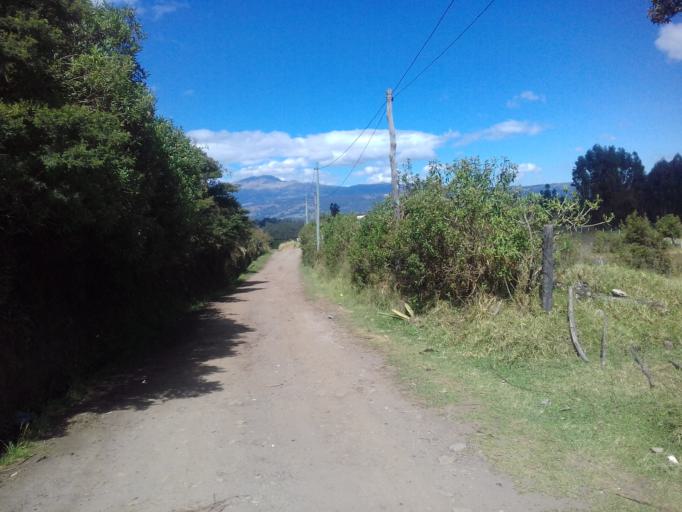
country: EC
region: Pichincha
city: Sangolqui
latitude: -0.3509
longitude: -78.4034
